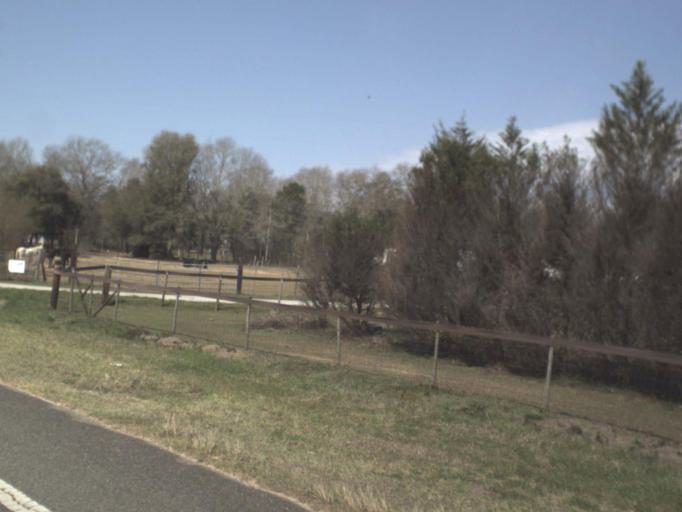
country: US
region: Florida
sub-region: Gadsden County
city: Havana
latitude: 30.6166
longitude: -84.4477
